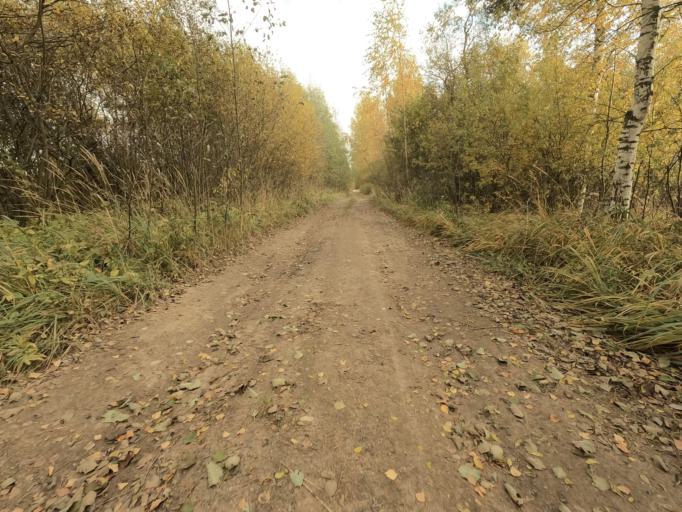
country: RU
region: Novgorod
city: Pankovka
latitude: 58.8798
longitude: 30.8103
